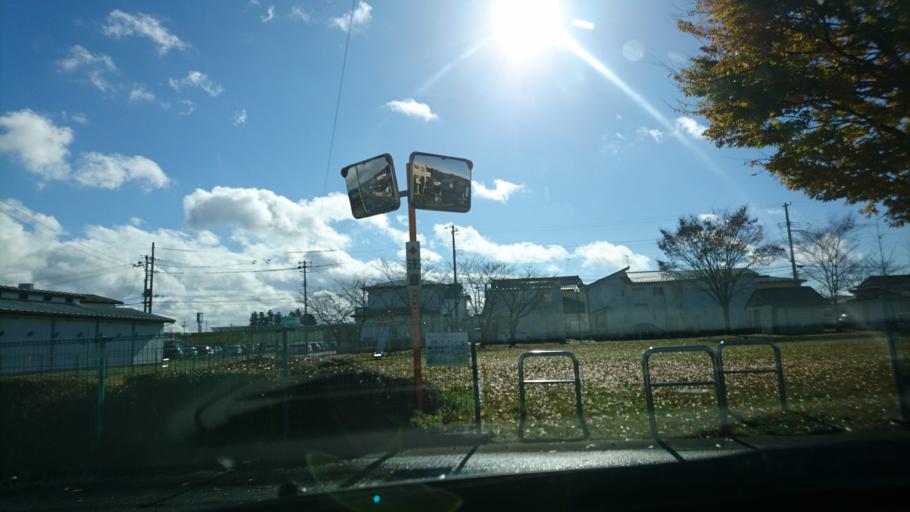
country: JP
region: Iwate
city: Ichinoseki
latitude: 38.9400
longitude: 141.1318
